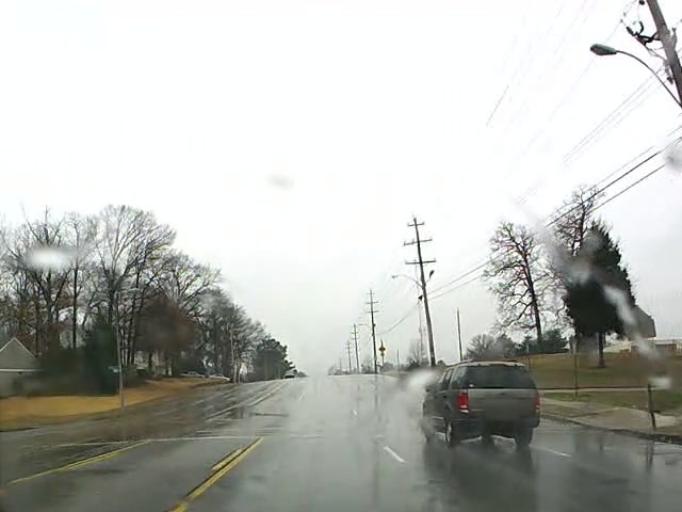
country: US
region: Tennessee
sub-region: Shelby County
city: Germantown
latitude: 35.0901
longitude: -89.8588
